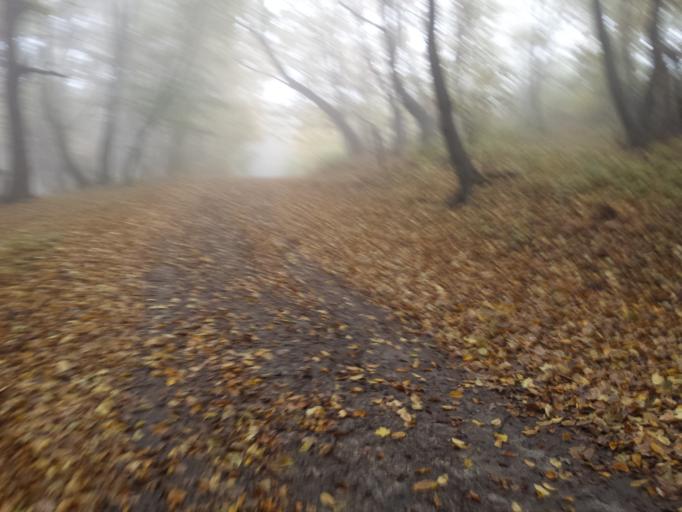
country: RO
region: Cluj
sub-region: Comuna Baciu
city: Baciu
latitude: 46.7748
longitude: 23.5496
